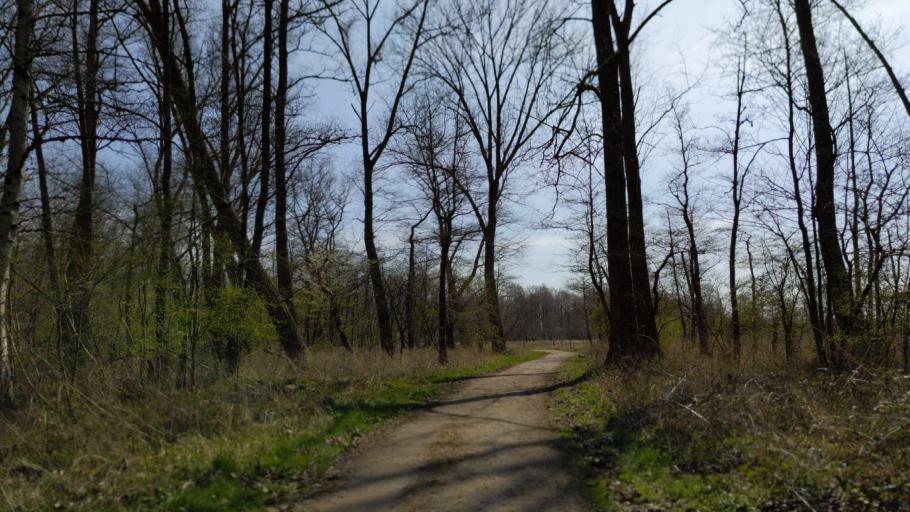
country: DE
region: Schleswig-Holstein
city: Travemuende
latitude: 53.9504
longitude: 10.8768
